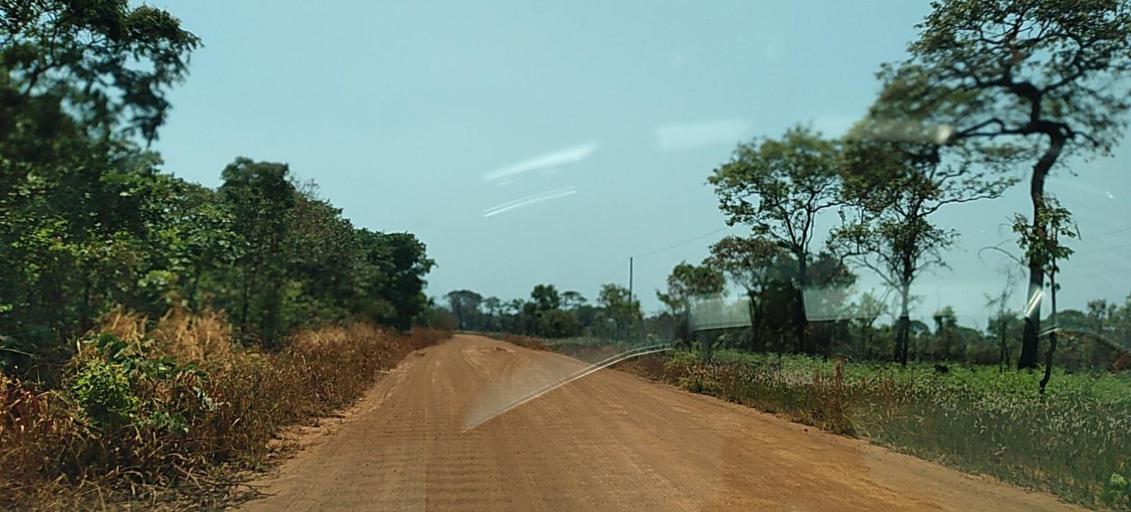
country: CD
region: Katanga
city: Kipushi
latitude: -11.9862
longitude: 26.8758
